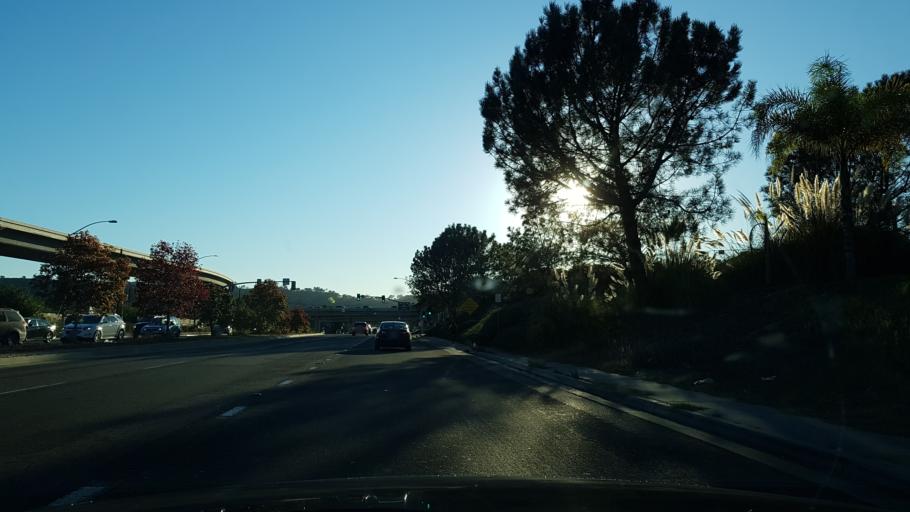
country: US
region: California
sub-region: San Diego County
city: Del Mar
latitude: 32.9342
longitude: -117.2383
